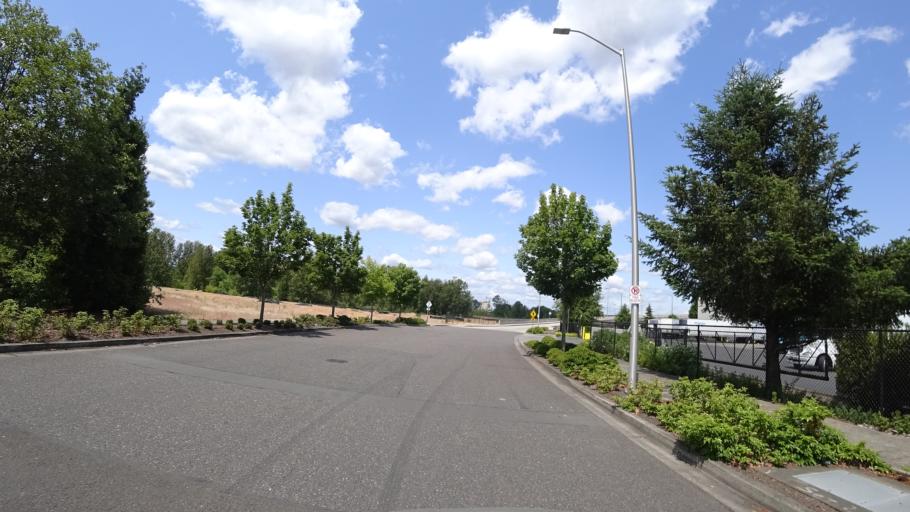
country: US
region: Washington
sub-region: Clark County
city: Lake Shore
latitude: 45.6327
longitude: -122.7567
